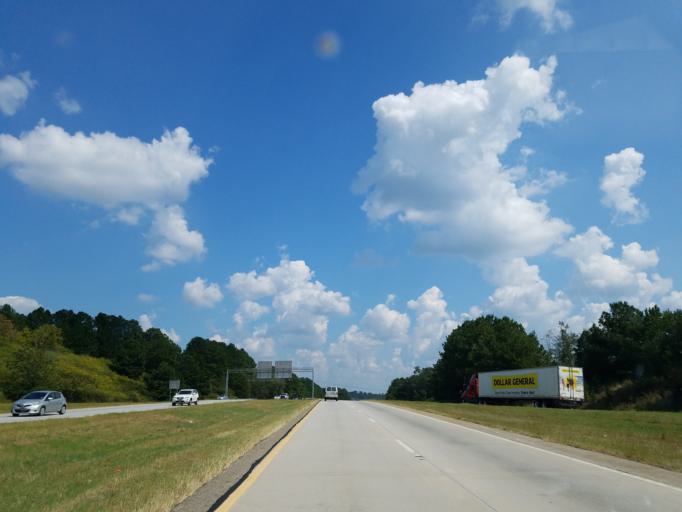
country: US
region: Georgia
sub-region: Clarke County
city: Athens
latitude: 33.9164
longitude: -83.4011
